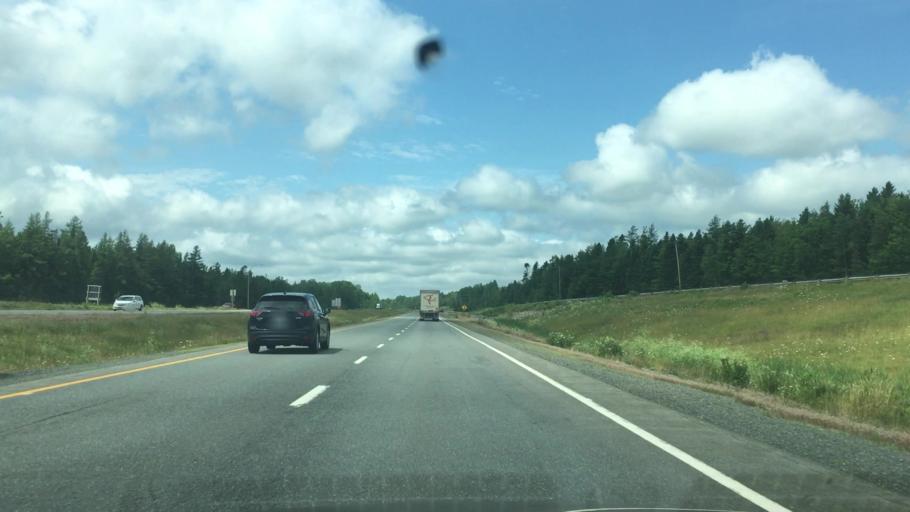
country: CA
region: Nova Scotia
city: Oxford
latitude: 45.7227
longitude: -63.8810
